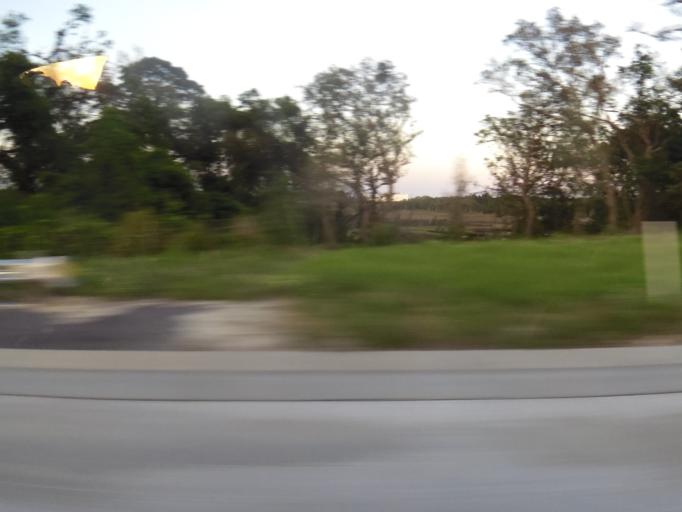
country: US
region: Florida
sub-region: Duval County
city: Jacksonville
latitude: 30.4042
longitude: -81.5639
